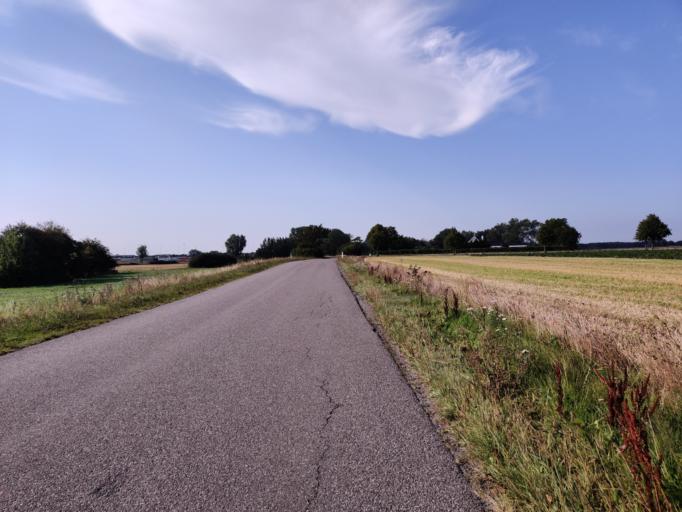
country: DK
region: Zealand
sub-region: Guldborgsund Kommune
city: Nykobing Falster
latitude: 54.7223
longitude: 11.9265
